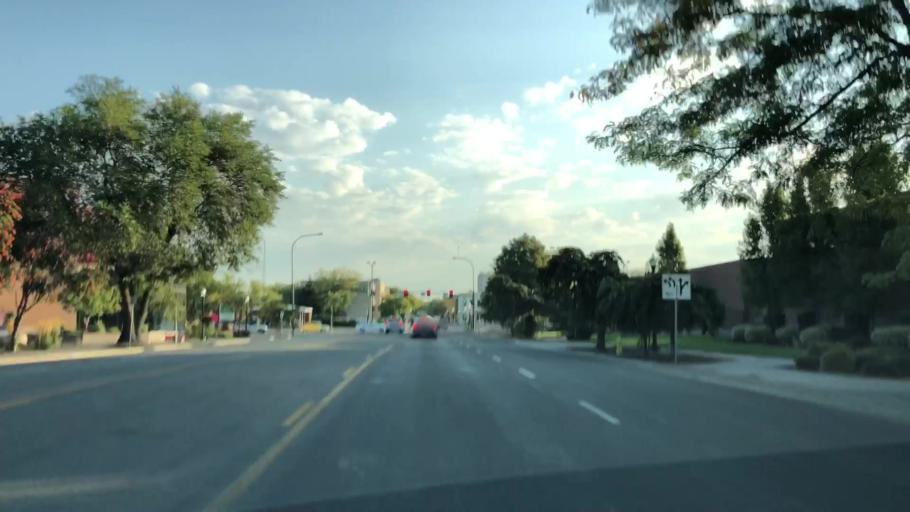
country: US
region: Idaho
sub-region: Bonneville County
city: Idaho Falls
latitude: 43.4912
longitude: -112.0434
